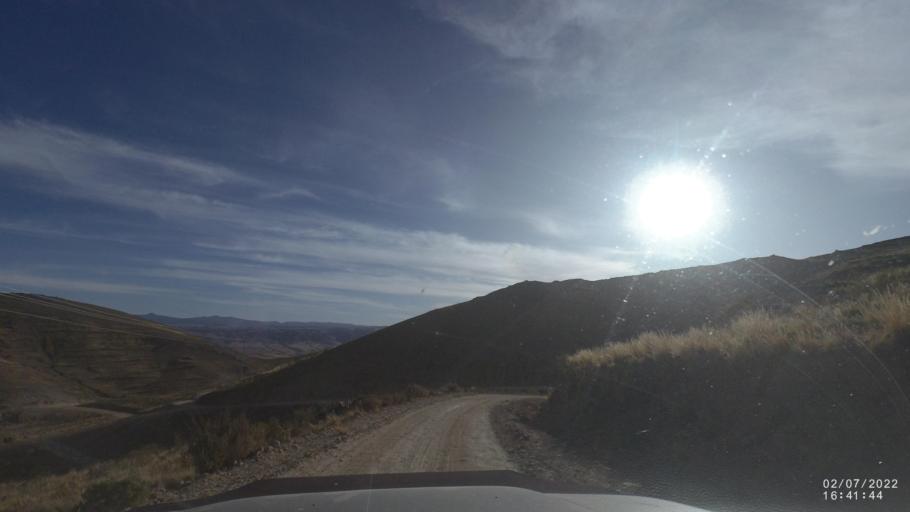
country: BO
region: Cochabamba
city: Irpa Irpa
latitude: -17.9723
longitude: -66.5024
